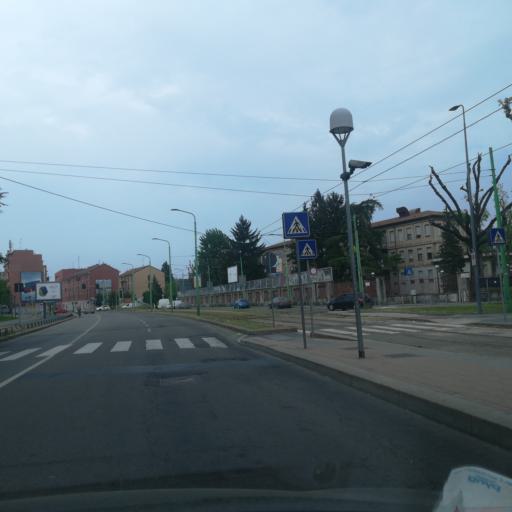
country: IT
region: Lombardy
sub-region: Citta metropolitana di Milano
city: Bresso
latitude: 45.5112
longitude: 9.1907
